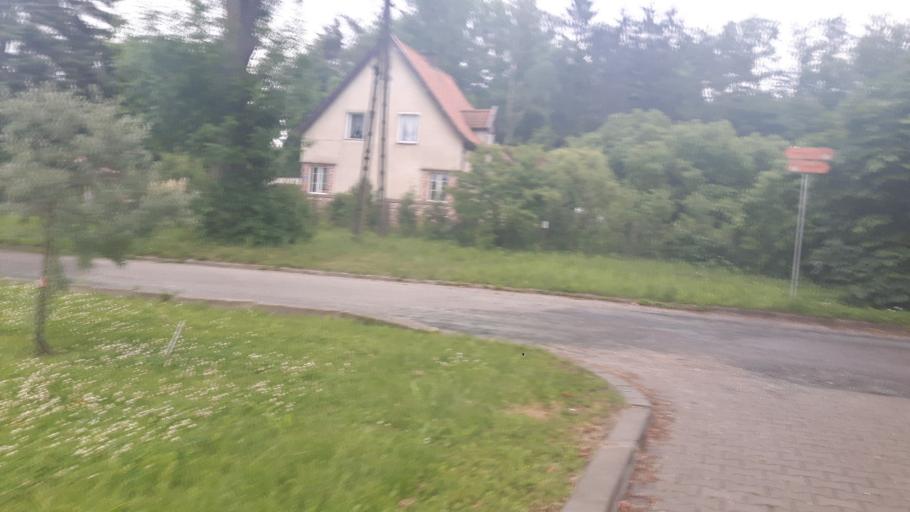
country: PL
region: Pomeranian Voivodeship
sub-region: Powiat nowodworski
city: Krynica Morska
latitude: 54.2831
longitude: 19.4349
